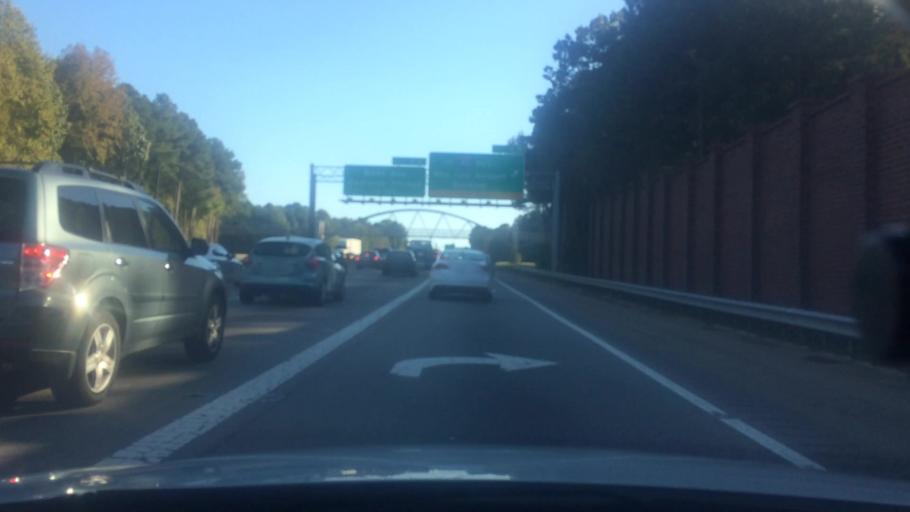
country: US
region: North Carolina
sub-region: Wake County
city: West Raleigh
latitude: 35.8082
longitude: -78.6941
